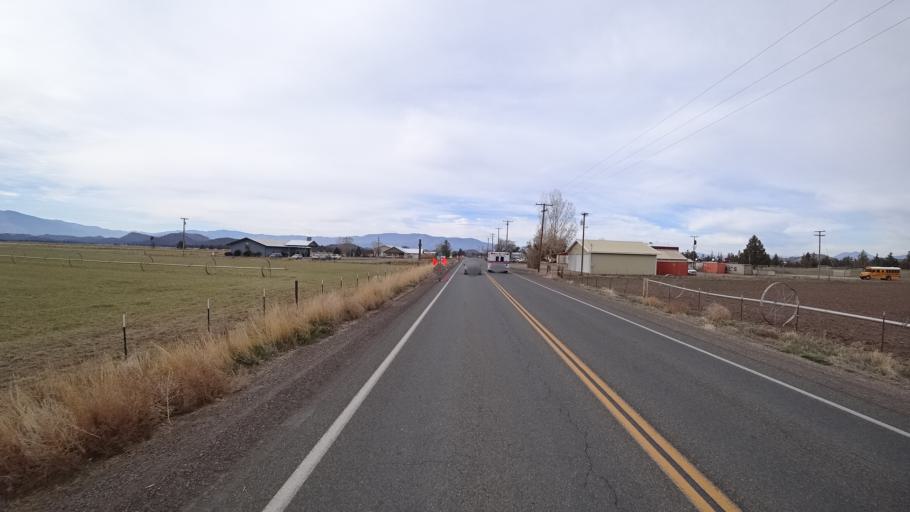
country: US
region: California
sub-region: Siskiyou County
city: Montague
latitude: 41.6239
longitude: -122.4039
